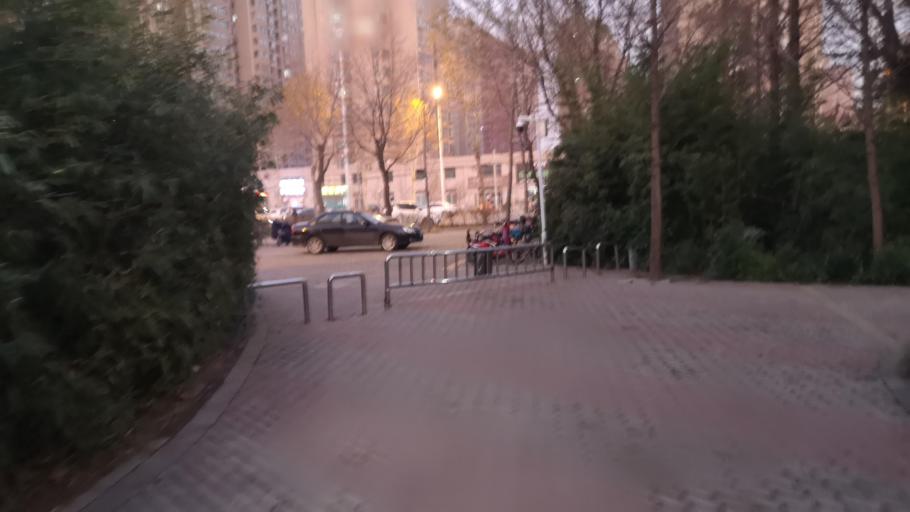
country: CN
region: Henan Sheng
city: Zhongyuanlu
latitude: 35.7450
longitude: 115.0648
